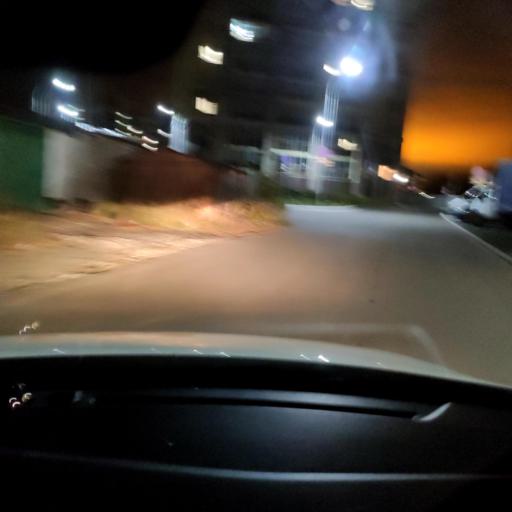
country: RU
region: Tatarstan
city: Staroye Arakchino
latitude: 55.8213
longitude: 49.0380
